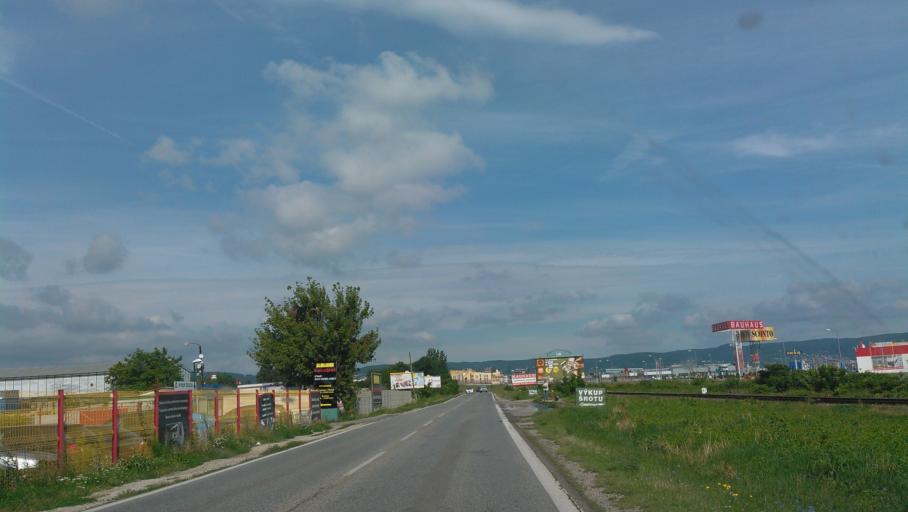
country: SK
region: Bratislavsky
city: Bratislava
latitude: 48.1578
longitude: 17.1897
